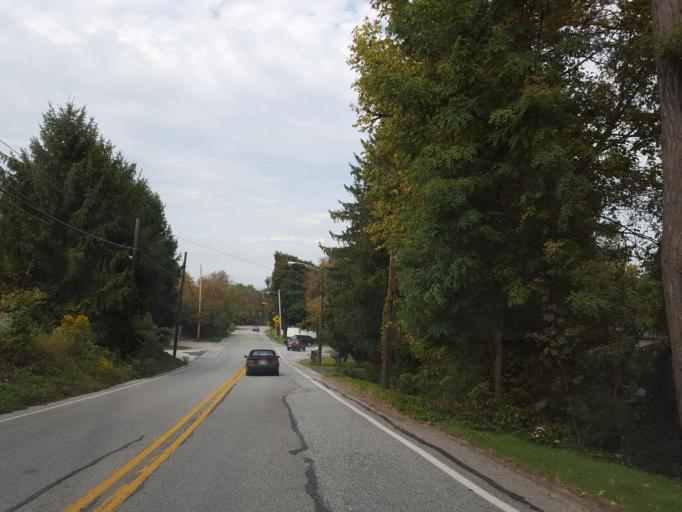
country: US
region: Pennsylvania
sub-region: York County
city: Valley View
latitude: 39.9546
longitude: -76.6967
